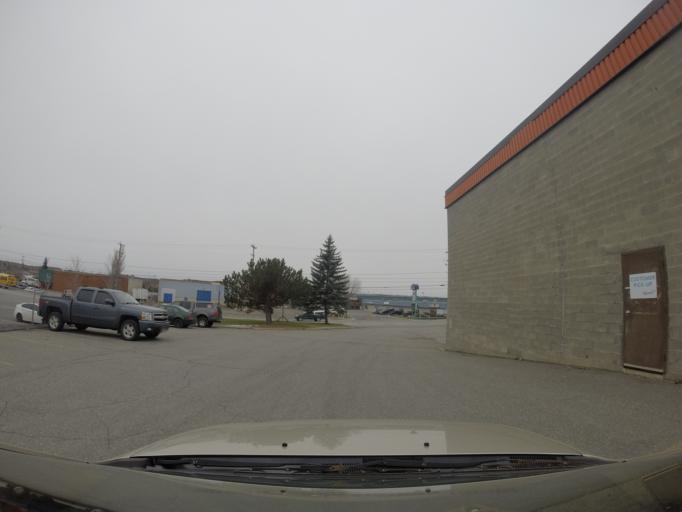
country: CA
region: Ontario
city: Greater Sudbury
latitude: 46.4653
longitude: -81.0293
